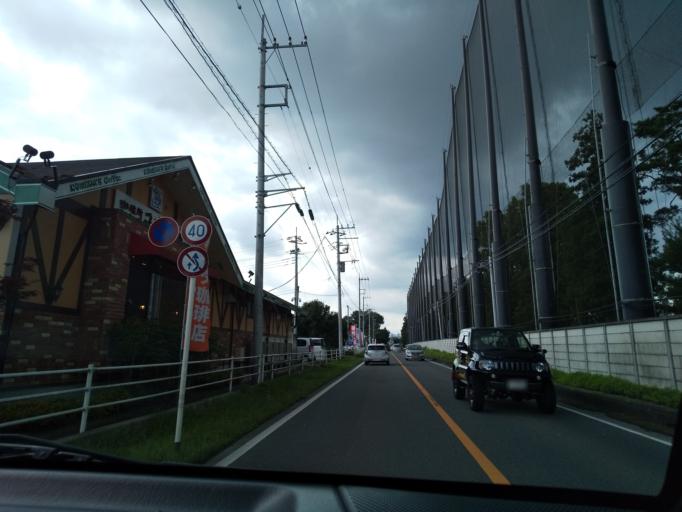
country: JP
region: Saitama
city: Hanno
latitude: 35.8591
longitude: 139.3522
